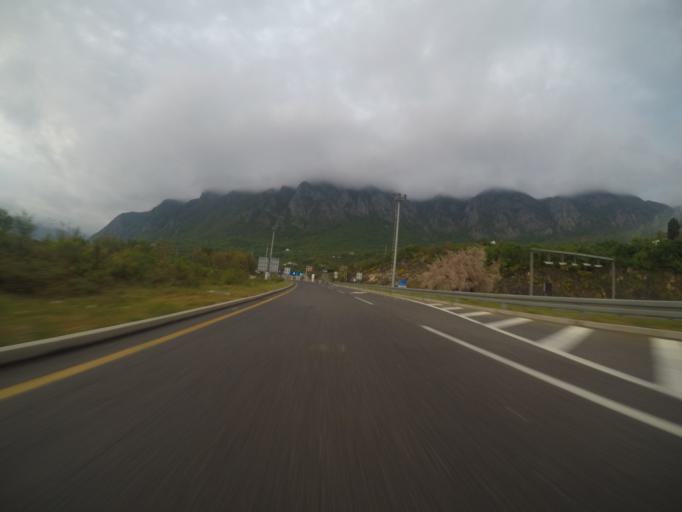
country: ME
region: Bar
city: Sutomore
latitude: 42.2028
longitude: 19.0508
